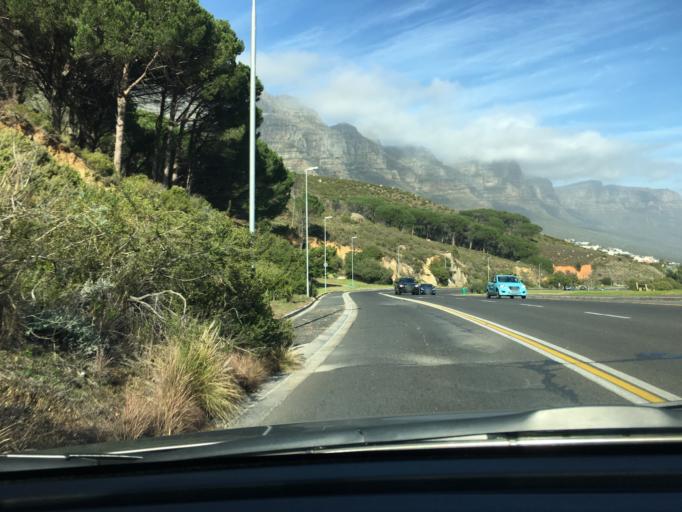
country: ZA
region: Western Cape
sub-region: City of Cape Town
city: Cape Town
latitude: -33.9452
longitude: 18.3924
